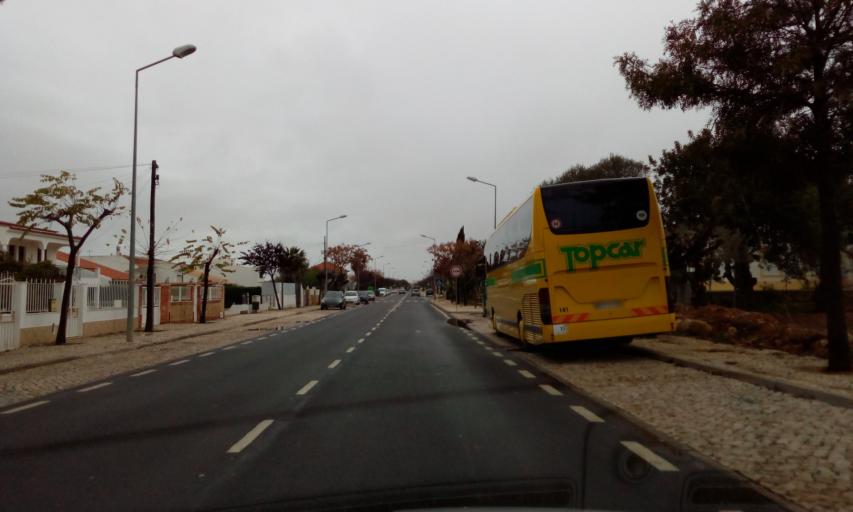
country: PT
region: Faro
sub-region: Albufeira
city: Ferreiras
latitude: 37.1246
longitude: -8.2257
